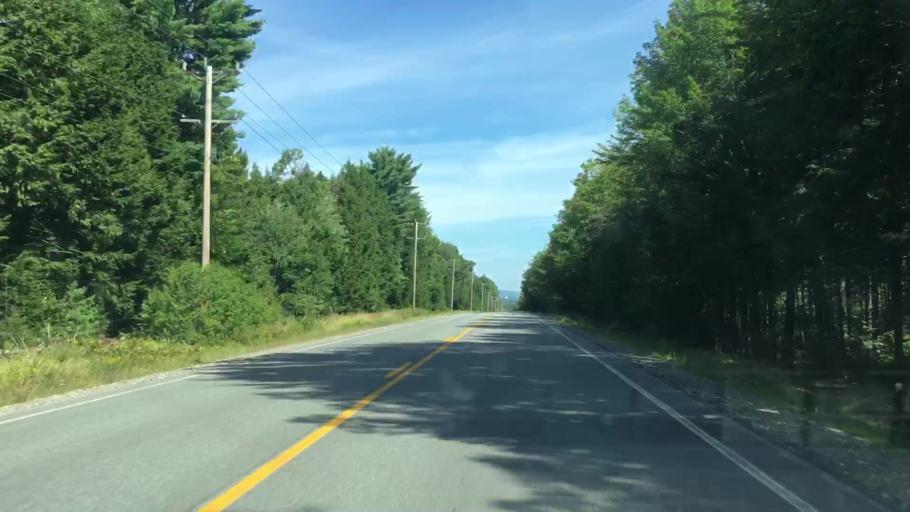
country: US
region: Maine
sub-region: Penobscot County
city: Howland
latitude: 45.2320
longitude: -68.7612
